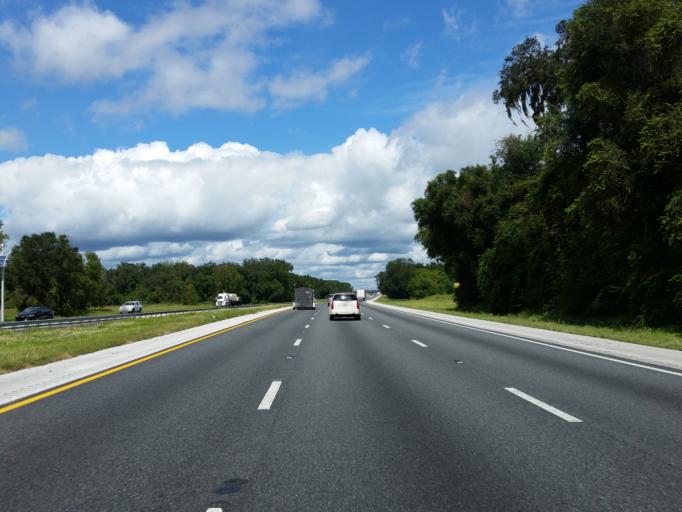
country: US
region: Florida
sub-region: Sumter County
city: Wildwood
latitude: 28.9195
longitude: -82.1119
